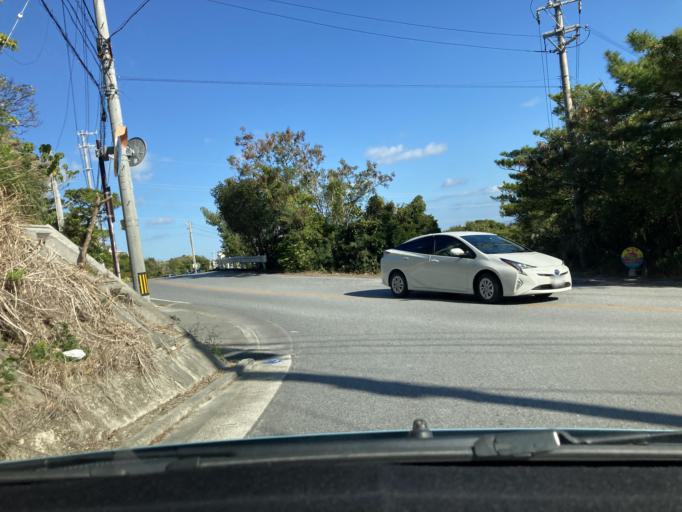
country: JP
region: Okinawa
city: Chatan
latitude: 26.3059
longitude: 127.7980
